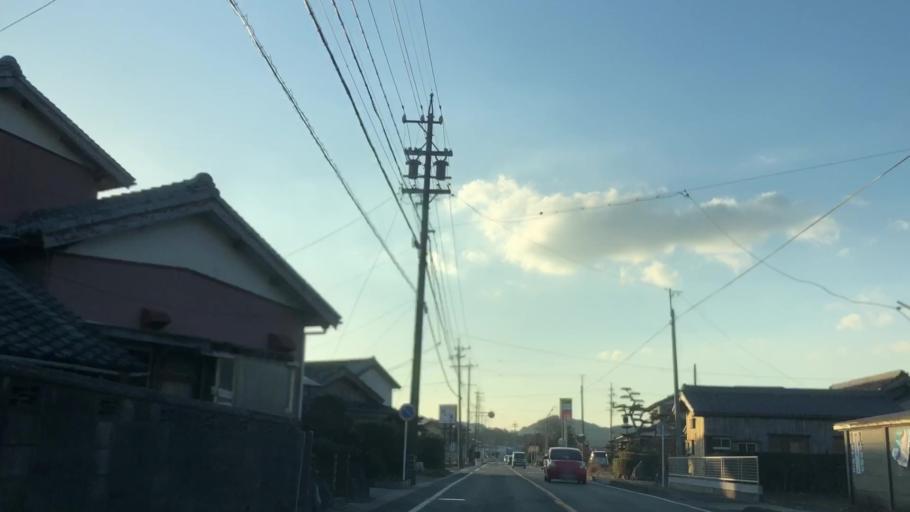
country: JP
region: Aichi
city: Tahara
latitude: 34.6538
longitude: 137.2112
